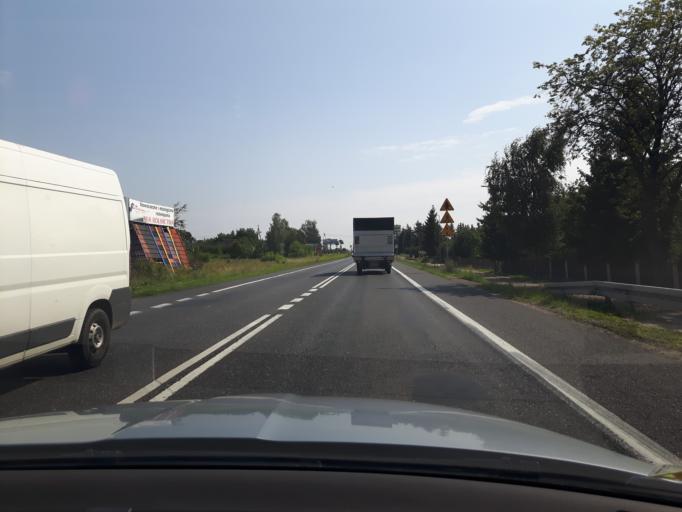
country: PL
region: Masovian Voivodeship
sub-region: Powiat mlawski
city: Mlawa
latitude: 53.1154
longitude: 20.3983
